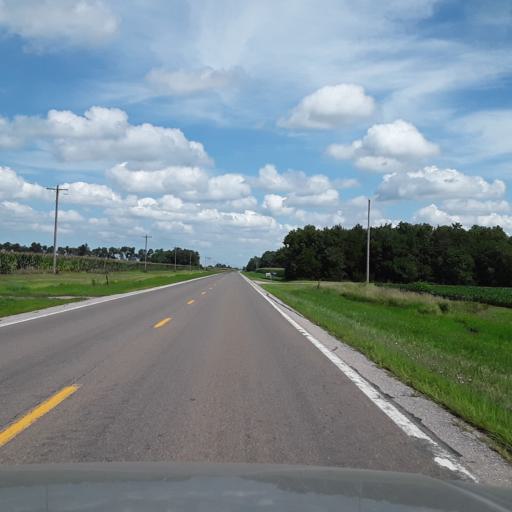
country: US
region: Nebraska
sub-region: Polk County
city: Osceola
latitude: 41.0999
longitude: -97.4261
